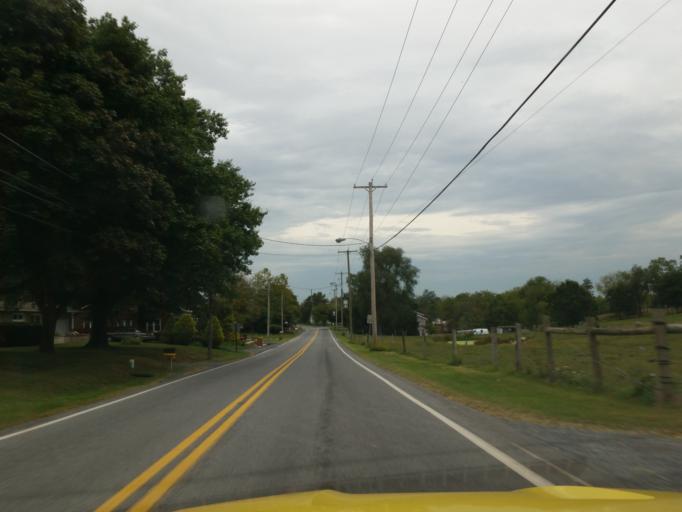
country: US
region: Pennsylvania
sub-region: Lebanon County
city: Myerstown
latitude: 40.4502
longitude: -76.3394
